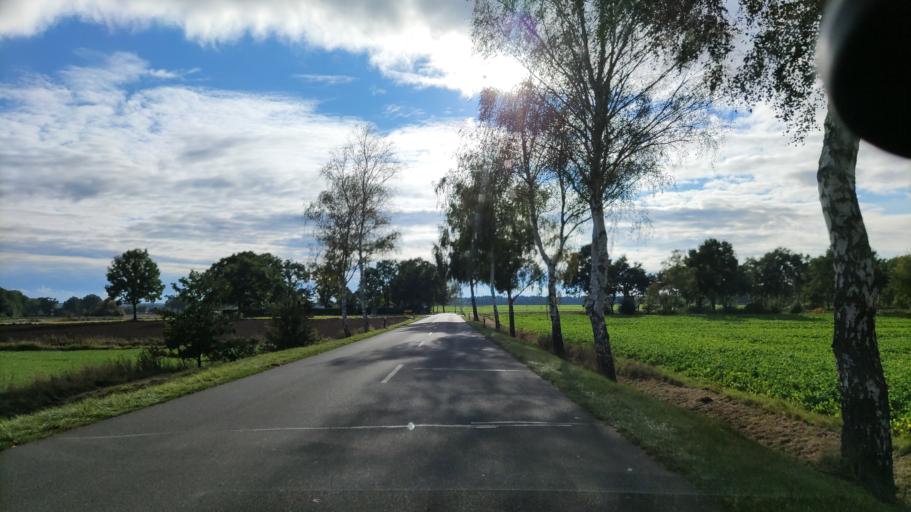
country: DE
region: Lower Saxony
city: Romstedt
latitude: 53.0843
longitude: 10.6386
